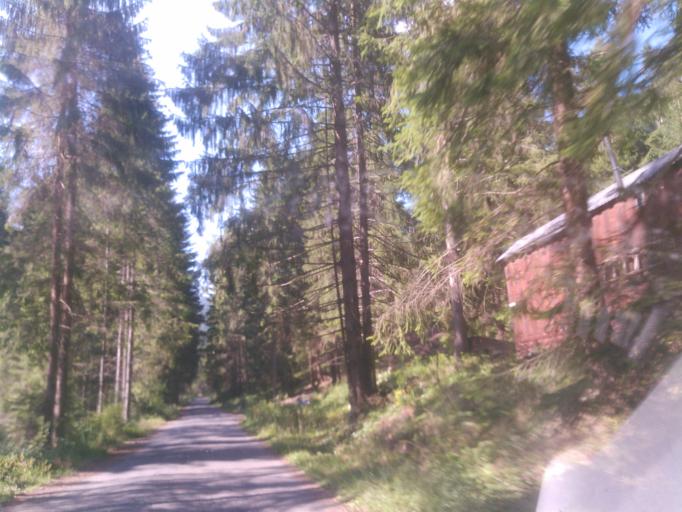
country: SK
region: Zilinsky
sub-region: Okres Liptovsky Mikulas
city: Liptovsky Mikulas
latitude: 49.0039
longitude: 19.5103
